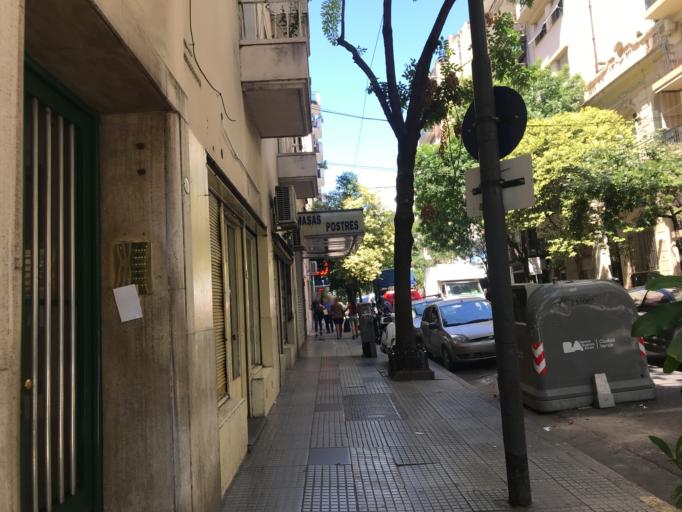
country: AR
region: Buenos Aires F.D.
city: Retiro
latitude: -34.6011
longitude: -58.3987
